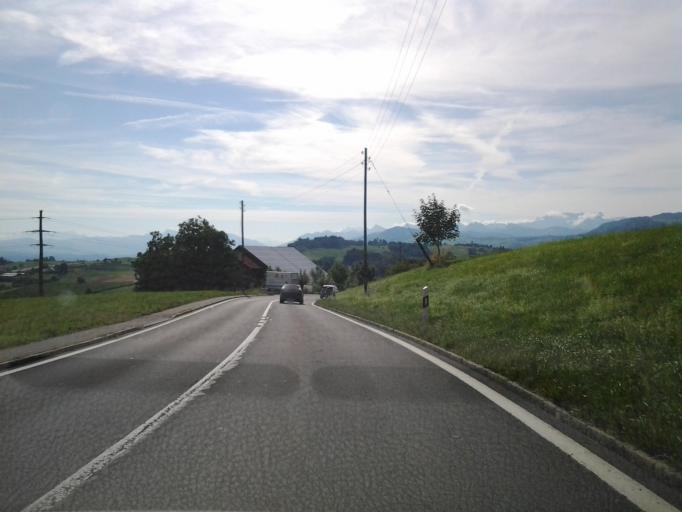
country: CH
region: Zurich
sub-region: Bezirk Horgen
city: Horgen / Allmend
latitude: 47.2287
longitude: 8.6160
